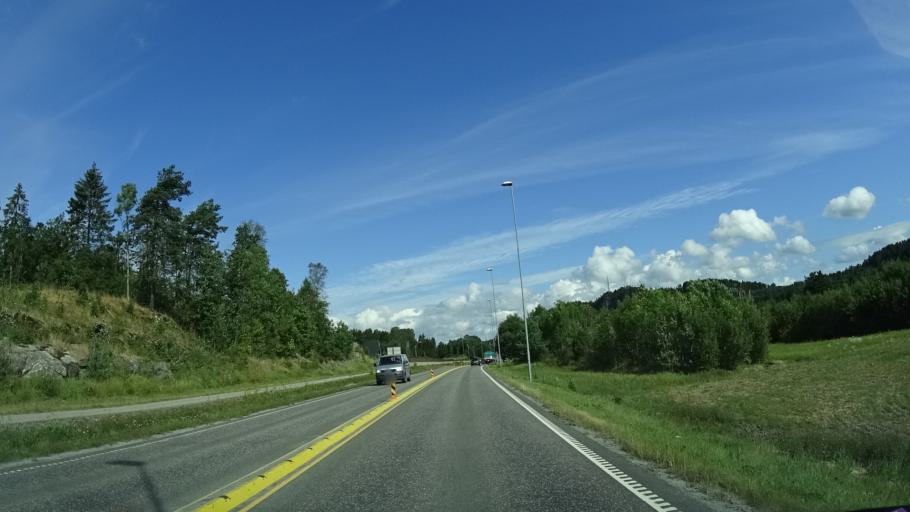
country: NO
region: Telemark
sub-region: Bamble
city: Langesund
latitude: 59.0315
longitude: 9.6782
